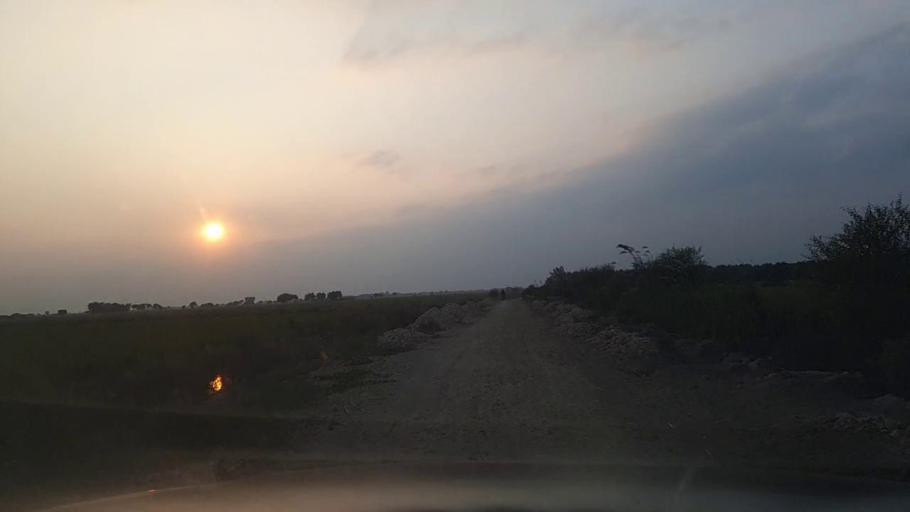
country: PK
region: Sindh
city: Jati
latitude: 24.5296
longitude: 68.4042
